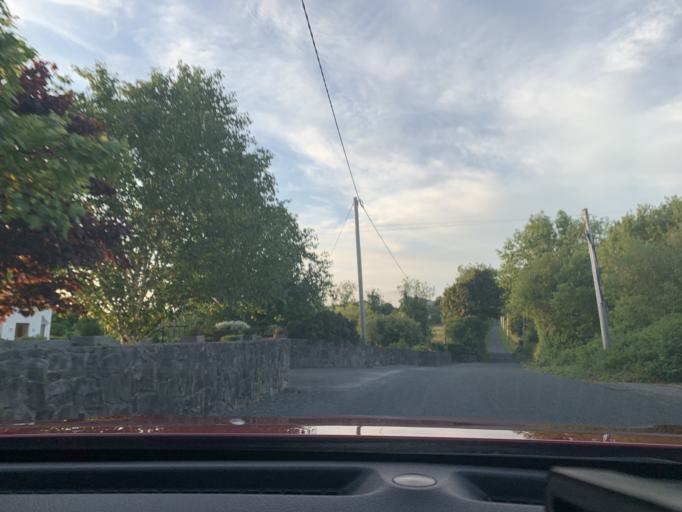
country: IE
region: Connaught
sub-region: Sligo
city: Sligo
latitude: 54.2831
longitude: -8.4332
